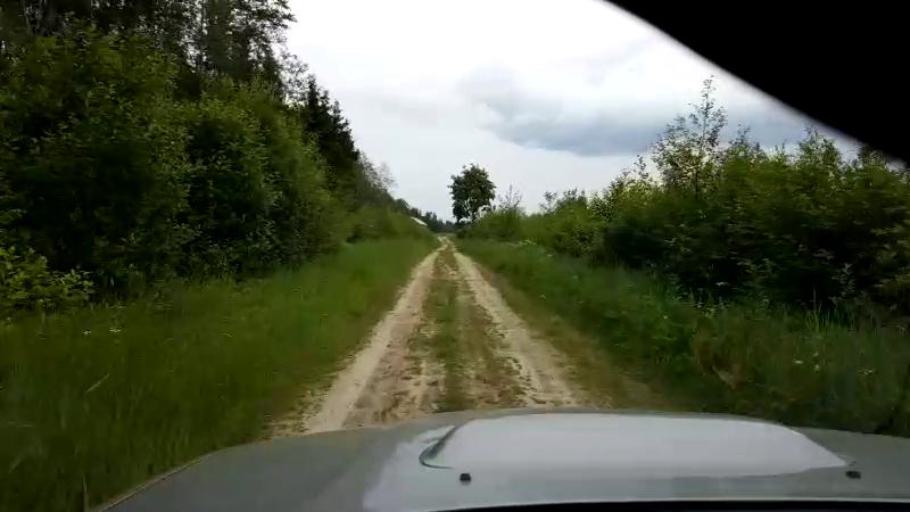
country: EE
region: Paernumaa
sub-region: Halinga vald
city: Parnu-Jaagupi
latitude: 58.5351
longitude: 24.6173
